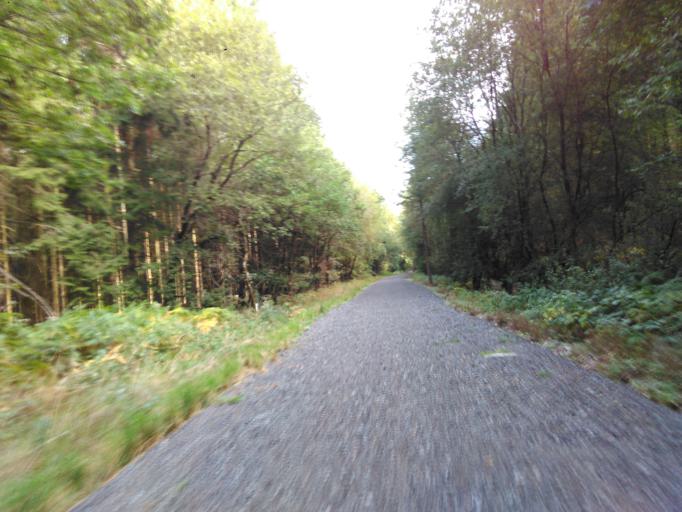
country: BE
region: Wallonia
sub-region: Province du Luxembourg
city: Vaux-sur-Sure
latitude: 49.9324
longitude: 5.5173
